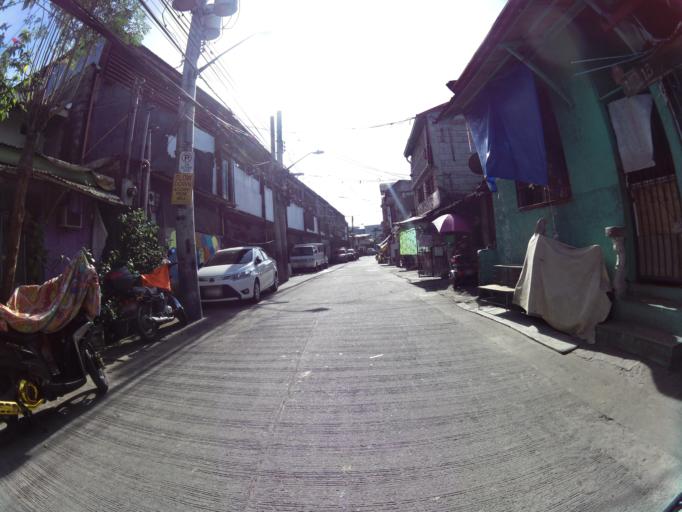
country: PH
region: Metro Manila
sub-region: Marikina
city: Calumpang
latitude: 14.6243
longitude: 121.0952
